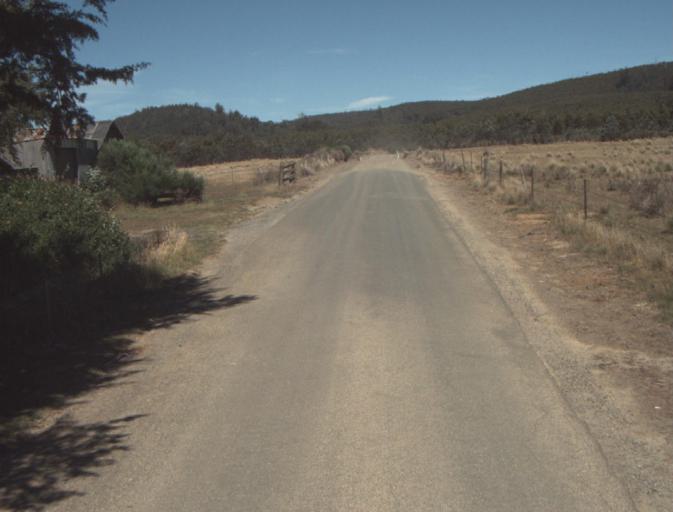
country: AU
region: Tasmania
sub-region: Dorset
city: Scottsdale
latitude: -41.3679
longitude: 147.4689
